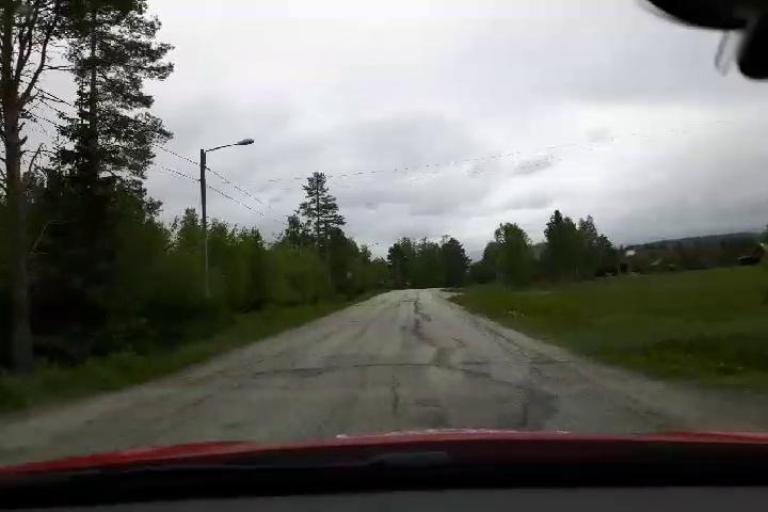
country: SE
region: Jaemtland
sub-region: Bergs Kommun
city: Hoverberg
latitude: 62.7388
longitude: 14.4230
